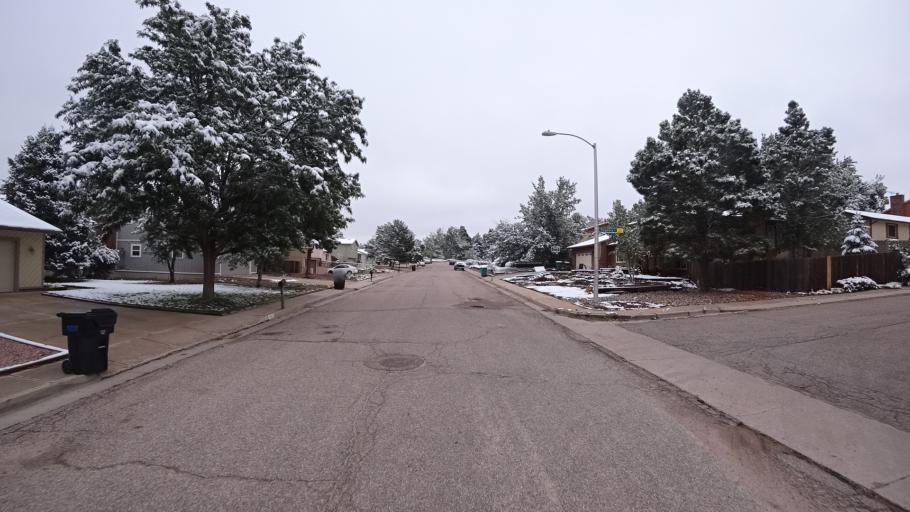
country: US
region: Colorado
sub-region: El Paso County
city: Cimarron Hills
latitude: 38.9234
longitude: -104.7736
